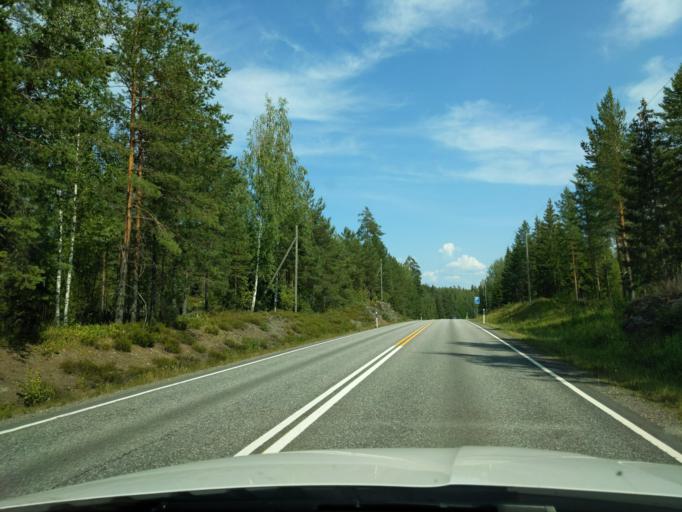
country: FI
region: Paijanne Tavastia
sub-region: Lahti
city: Padasjoki
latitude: 61.3279
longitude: 25.1964
